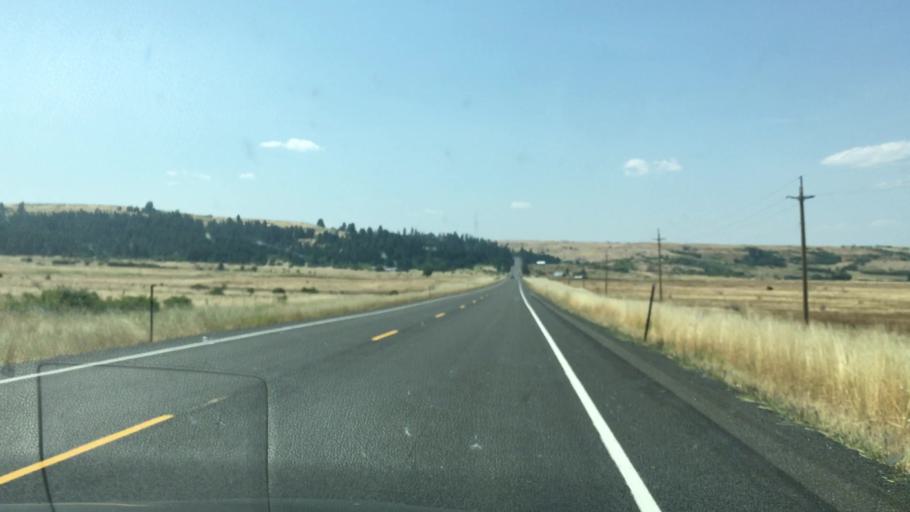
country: US
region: Idaho
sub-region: Idaho County
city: Grangeville
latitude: 45.8855
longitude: -116.2064
